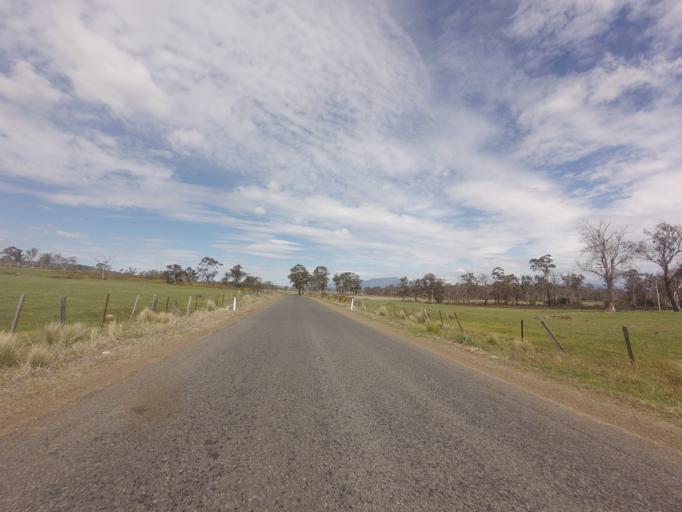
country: AU
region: Tasmania
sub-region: Northern Midlands
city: Longford
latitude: -41.7304
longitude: 147.1959
